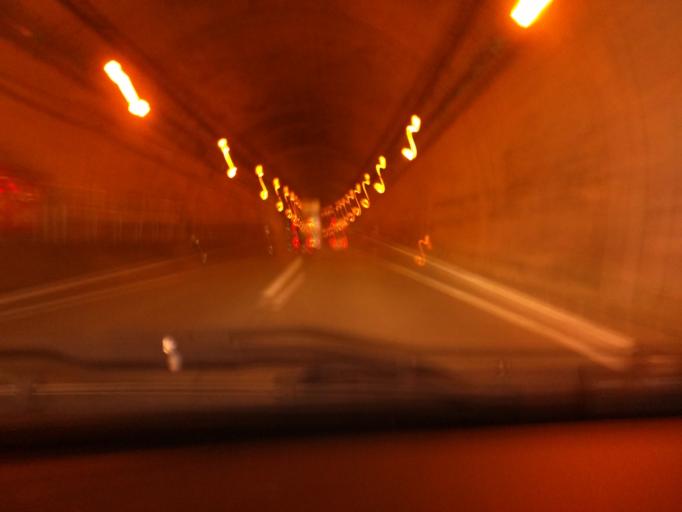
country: JP
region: Niigata
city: Kashiwazaki
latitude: 37.3381
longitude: 138.5367
